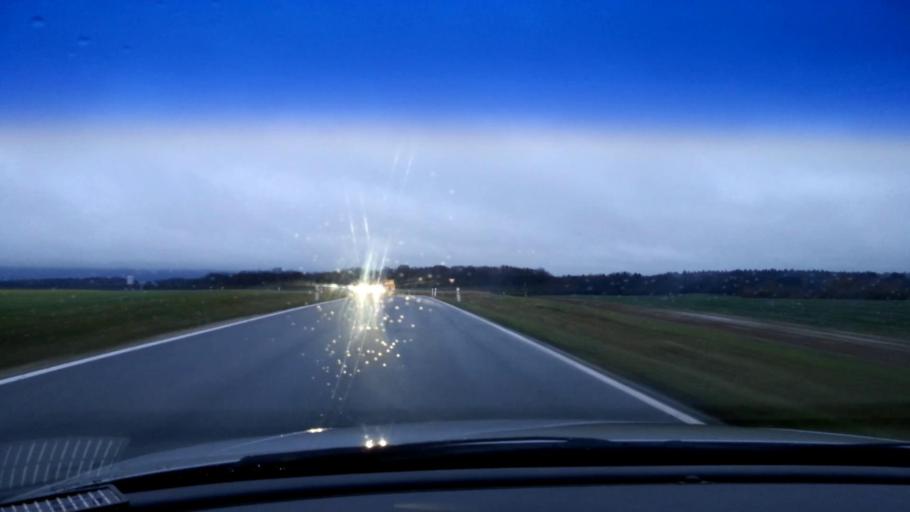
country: DE
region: Bavaria
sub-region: Upper Franconia
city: Zapfendorf
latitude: 49.9857
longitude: 10.9543
